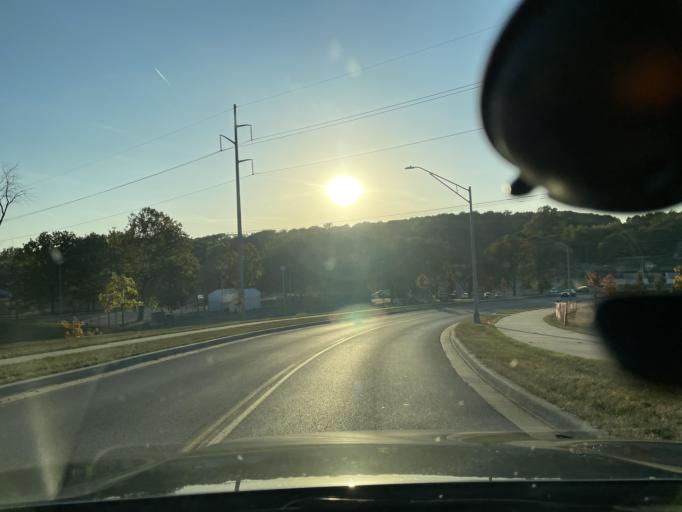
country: US
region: Missouri
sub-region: Buchanan County
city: Saint Joseph
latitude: 39.7979
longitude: -94.8419
